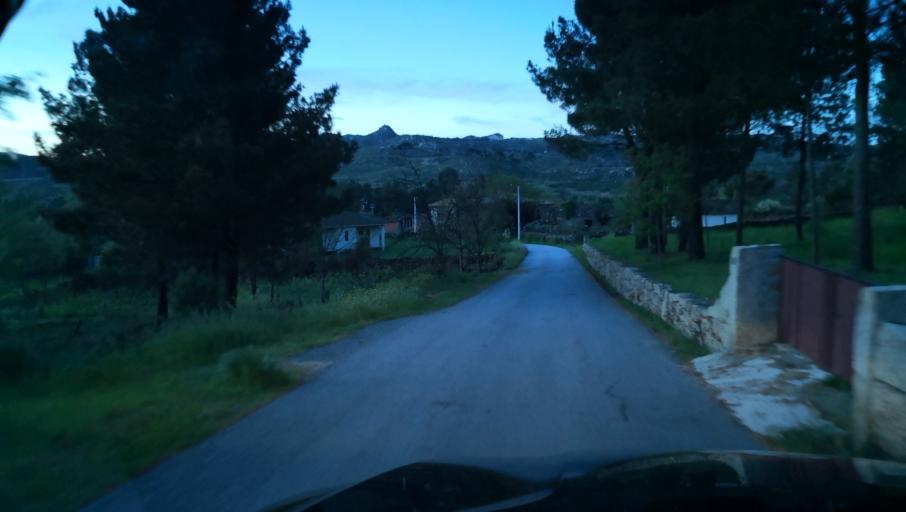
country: PT
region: Vila Real
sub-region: Vila Real
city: Vila Real
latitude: 41.3532
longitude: -7.6899
